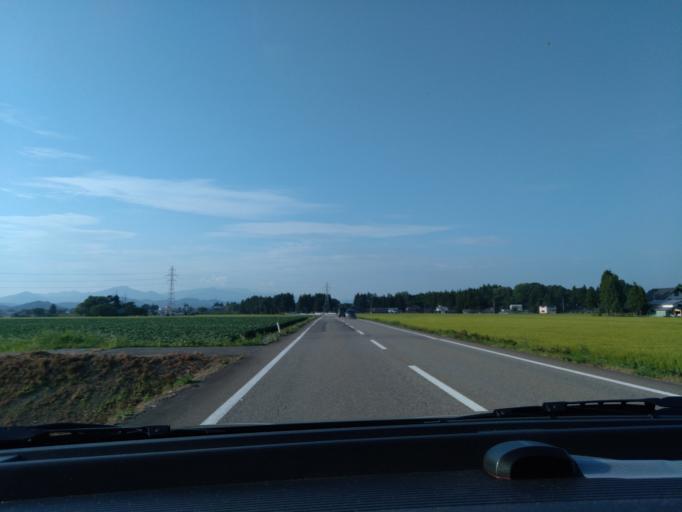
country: JP
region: Akita
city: Kakunodatemachi
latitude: 39.5350
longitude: 140.5582
